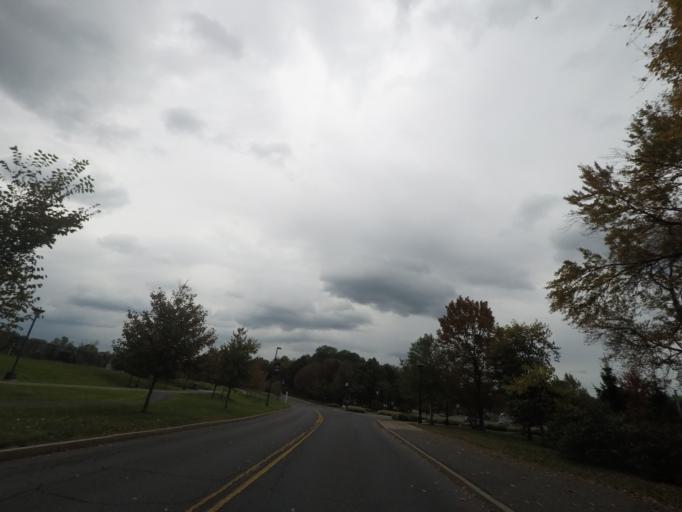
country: US
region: New York
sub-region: Albany County
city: McKownville
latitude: 42.6786
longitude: -73.8275
